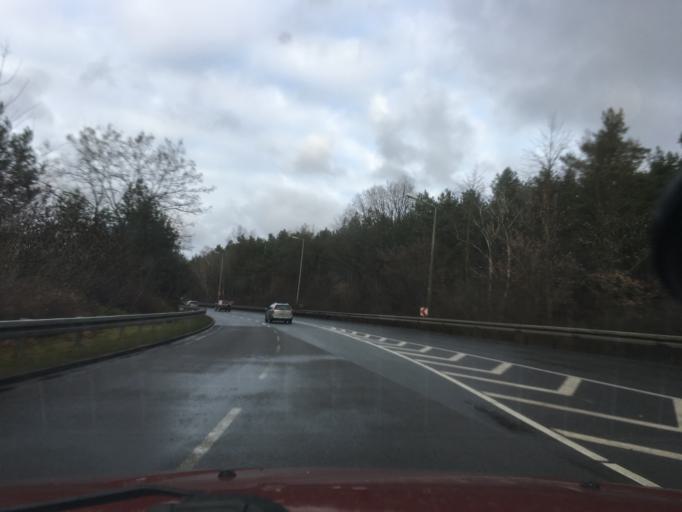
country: DE
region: Berlin
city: Grunau
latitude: 52.4179
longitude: 13.5694
